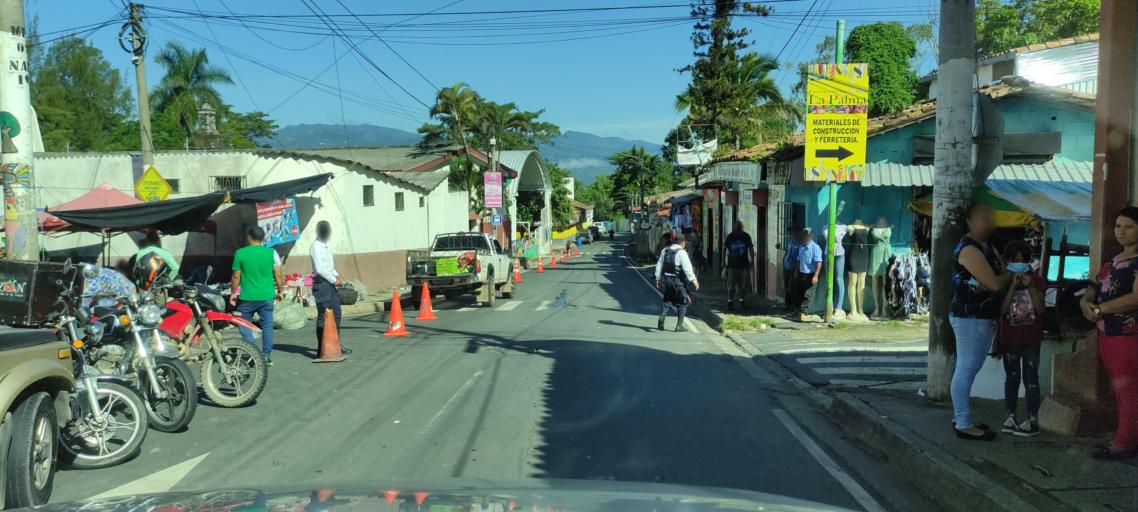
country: HN
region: Ocotepeque
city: Antigua Ocotepeque
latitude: 14.3168
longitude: -89.1699
